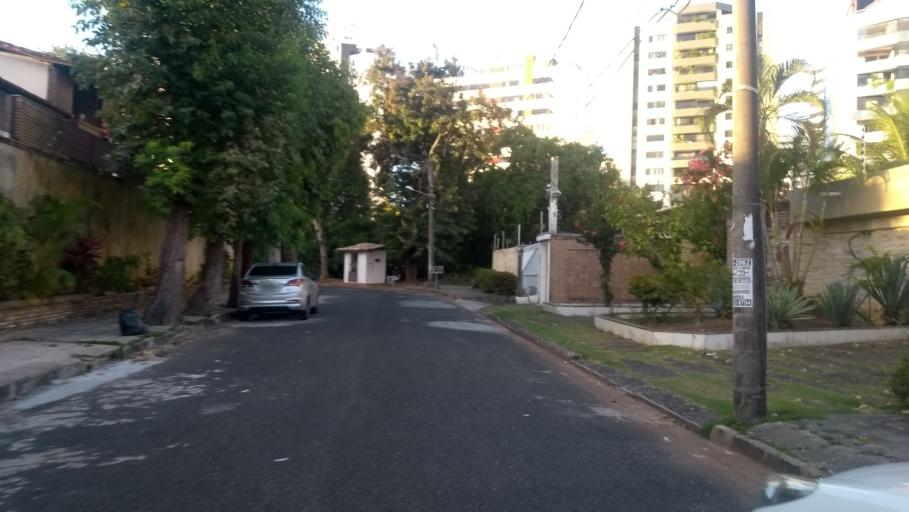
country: BR
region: Bahia
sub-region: Salvador
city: Salvador
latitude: -12.9902
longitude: -38.4629
